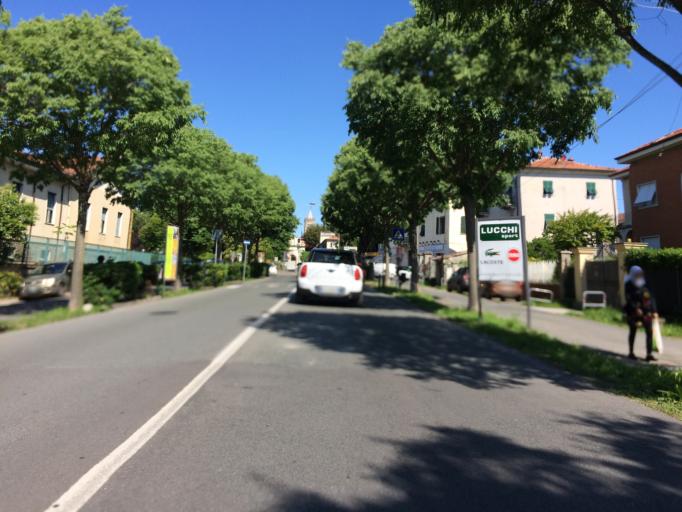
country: IT
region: Liguria
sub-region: Provincia di La Spezia
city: Sarzana
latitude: 44.1095
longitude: 9.9662
